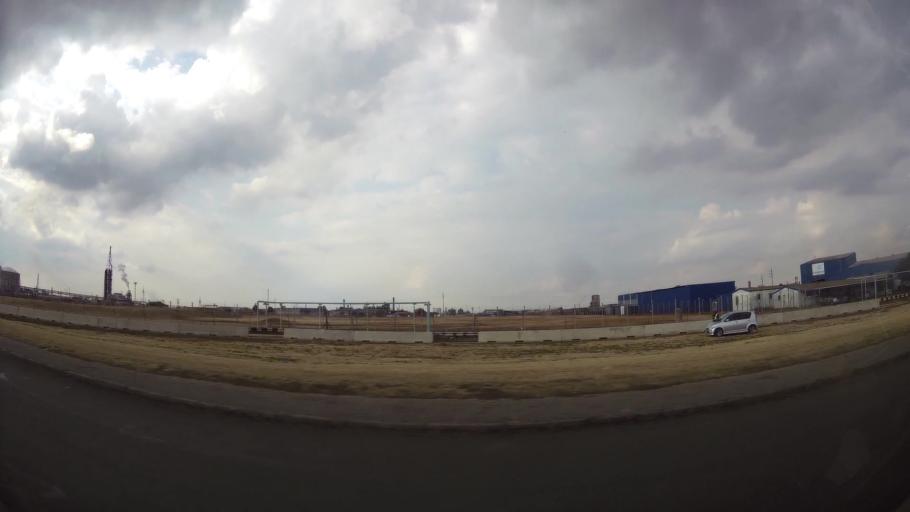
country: ZA
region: Orange Free State
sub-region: Fezile Dabi District Municipality
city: Sasolburg
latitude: -26.8309
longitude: 27.8596
